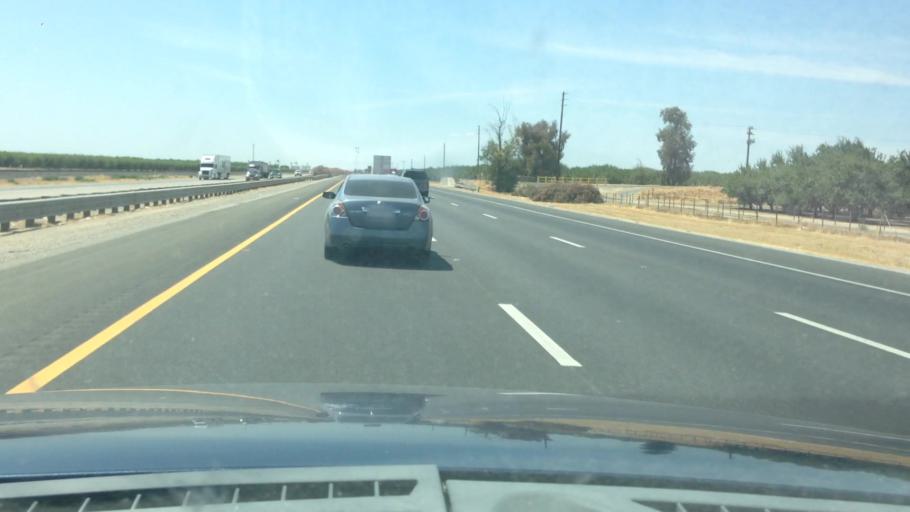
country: US
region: California
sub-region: Kern County
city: McFarland
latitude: 35.6324
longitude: -119.2165
